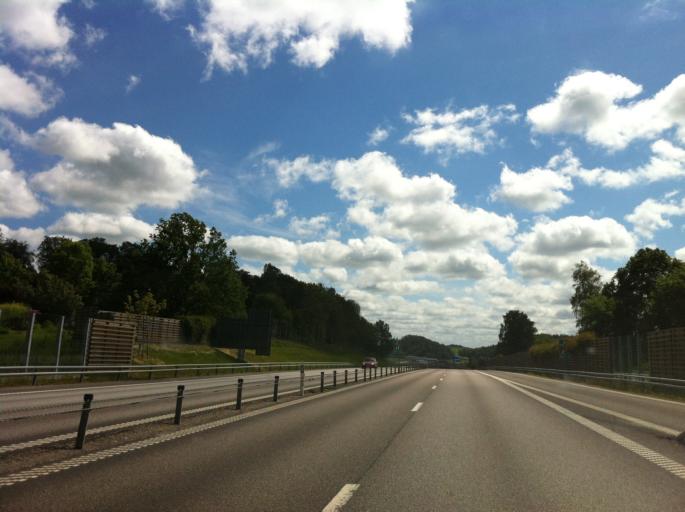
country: SE
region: Vaestra Goetaland
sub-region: Lilla Edets Kommun
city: Lilla Edet
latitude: 58.1305
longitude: 12.1361
